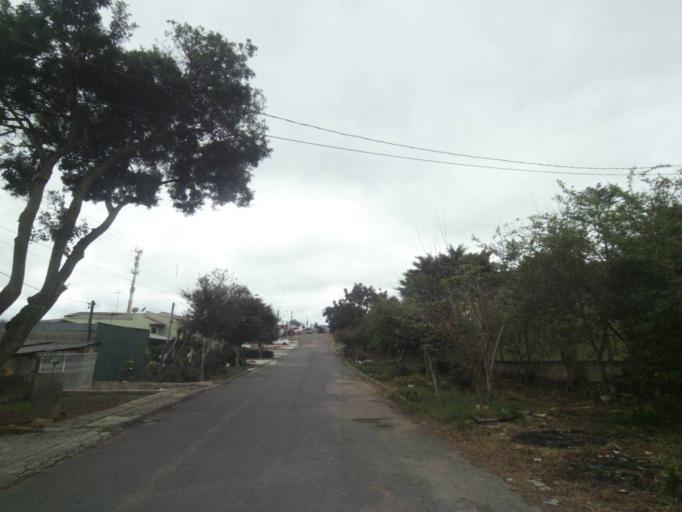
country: BR
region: Parana
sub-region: Sao Jose Dos Pinhais
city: Sao Jose dos Pinhais
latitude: -25.5381
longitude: -49.2998
